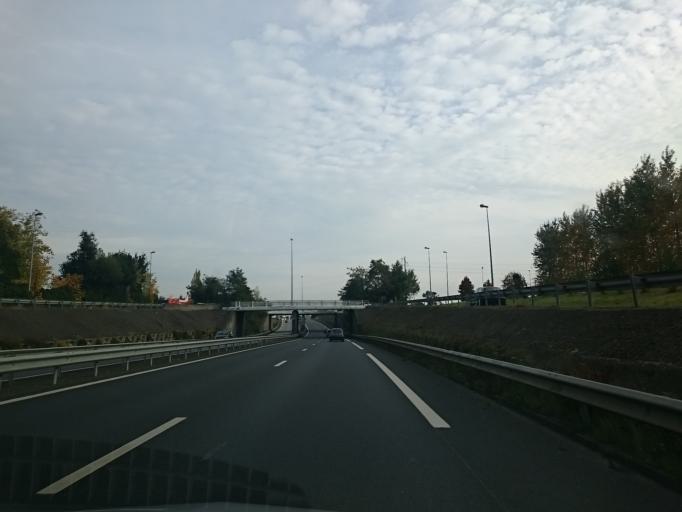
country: FR
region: Brittany
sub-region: Departement d'Ille-et-Vilaine
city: Chantepie
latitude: 48.0644
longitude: -1.6190
